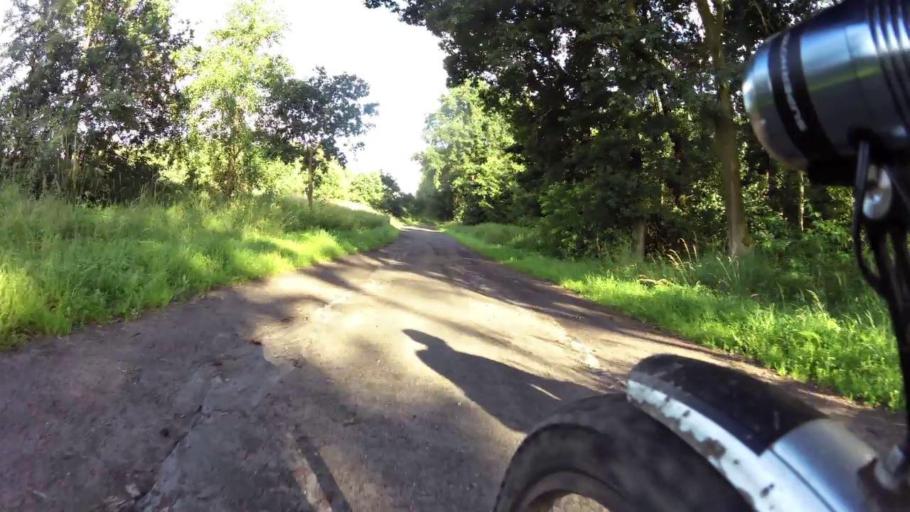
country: PL
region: West Pomeranian Voivodeship
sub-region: Powiat swidwinski
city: Swidwin
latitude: 53.7654
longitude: 15.8797
